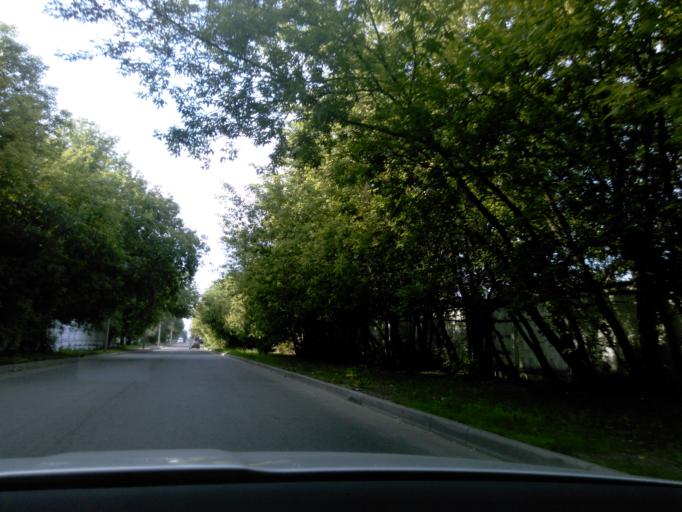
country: RU
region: Moskovskaya
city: Levoberezhnaya
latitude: 55.8750
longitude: 37.4706
